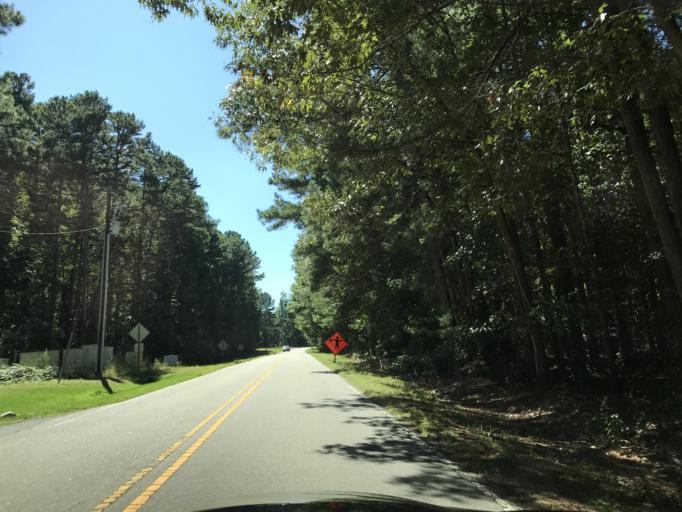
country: US
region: North Carolina
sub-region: Wake County
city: Wake Forest
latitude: 35.9497
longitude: -78.6359
